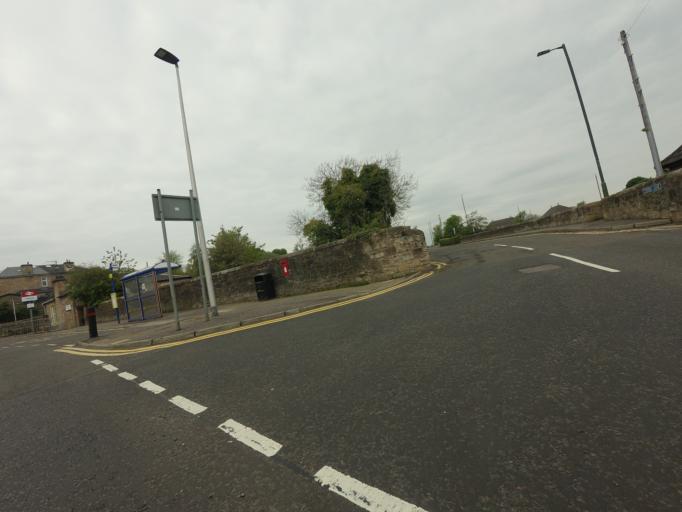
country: GB
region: Scotland
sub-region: Falkirk
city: Polmont
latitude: 55.9849
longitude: -3.7146
